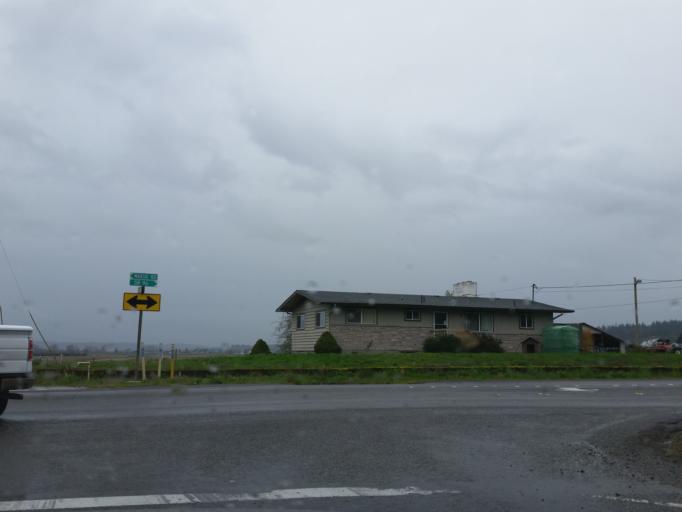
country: US
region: Washington
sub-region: Snohomish County
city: Silver Firs
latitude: 47.8920
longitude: -122.1447
